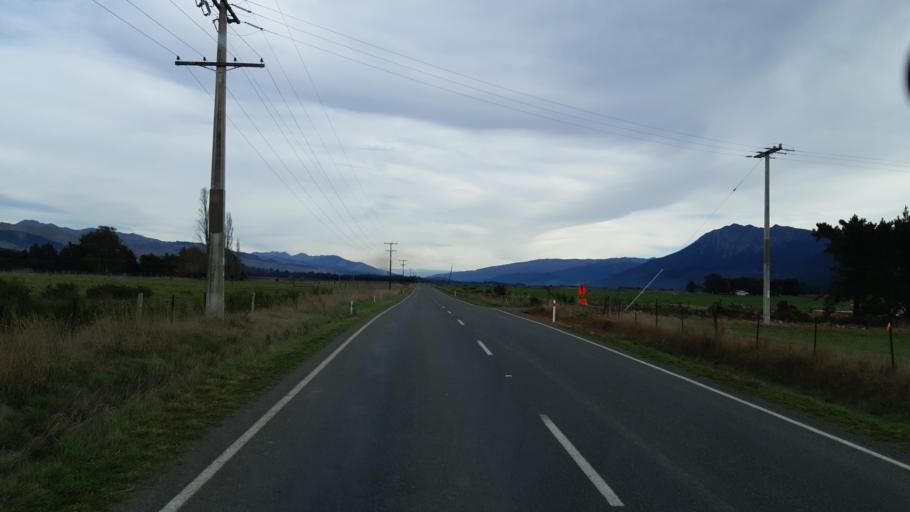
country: NZ
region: Tasman
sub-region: Tasman District
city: Richmond
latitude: -41.6094
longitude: 173.3992
